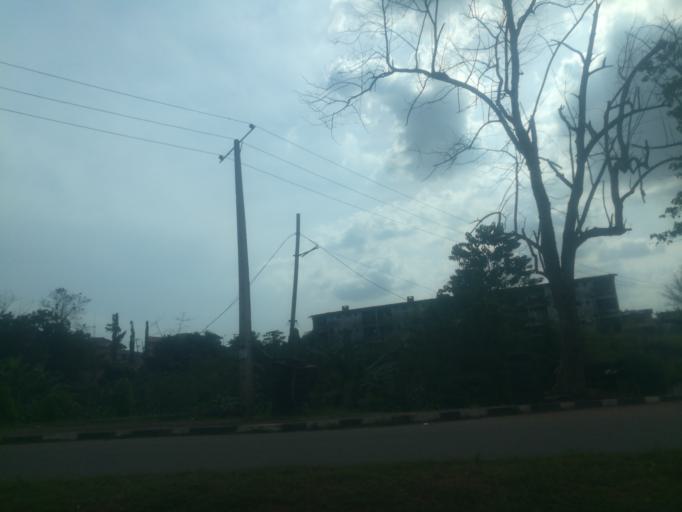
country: NG
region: Ogun
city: Abeokuta
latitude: 7.1364
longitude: 3.3452
